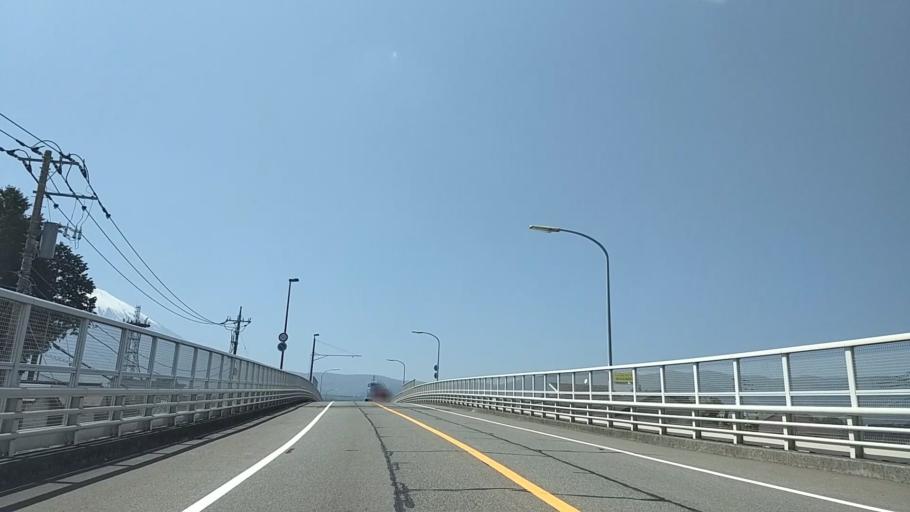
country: JP
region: Shizuoka
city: Gotemba
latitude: 35.3021
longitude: 138.9376
